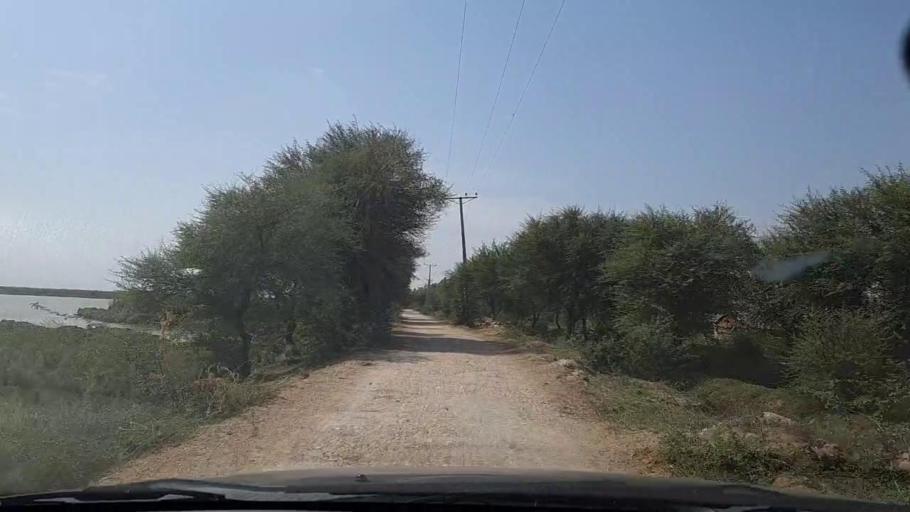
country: PK
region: Sindh
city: Mirpur Batoro
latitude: 24.6100
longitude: 68.2411
